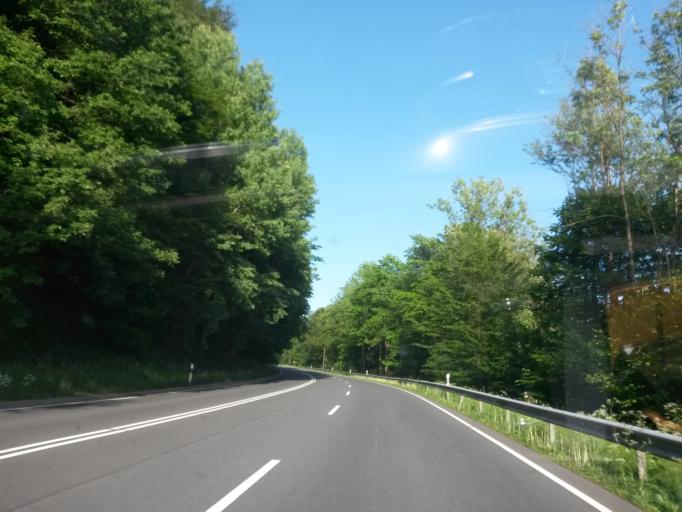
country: DE
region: North Rhine-Westphalia
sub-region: Regierungsbezirk Arnsberg
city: Drolshagen
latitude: 51.0455
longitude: 7.7297
